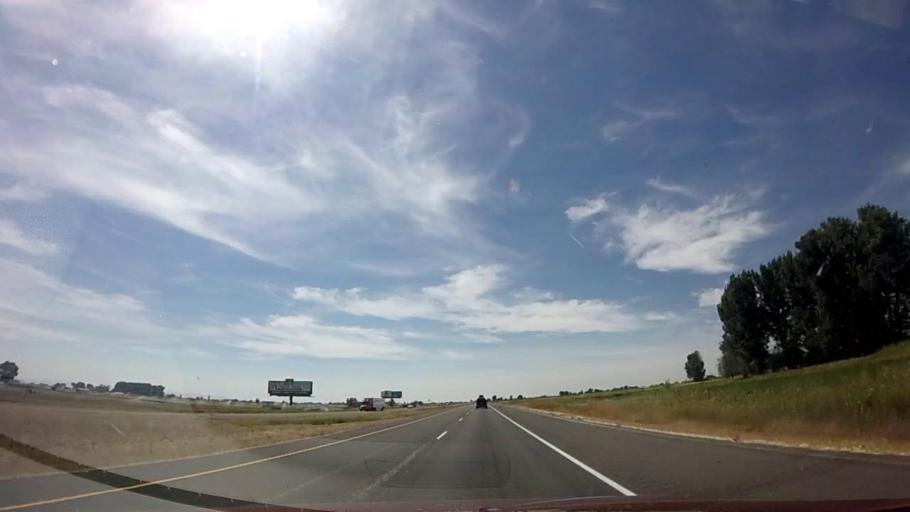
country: US
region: Idaho
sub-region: Minidoka County
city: Rupert
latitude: 42.5692
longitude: -113.7064
